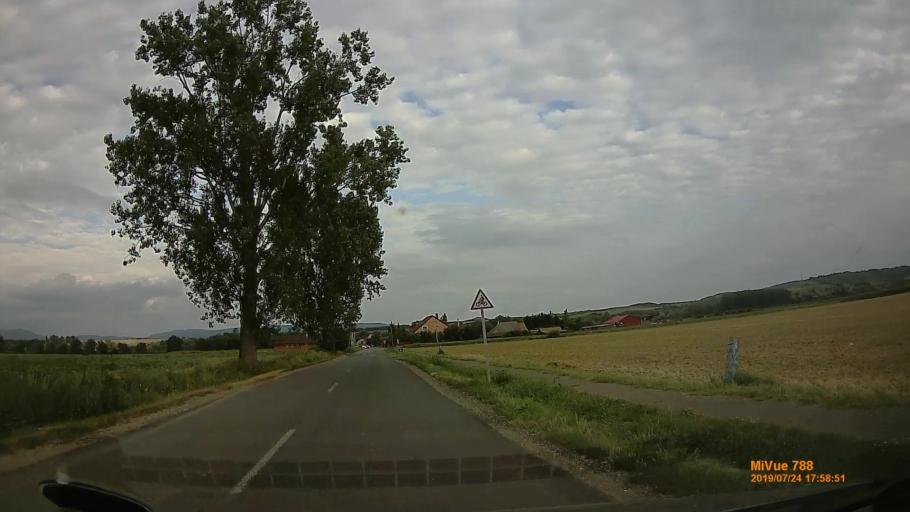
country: HU
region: Borsod-Abauj-Zemplen
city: Encs
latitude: 48.3212
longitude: 21.1517
